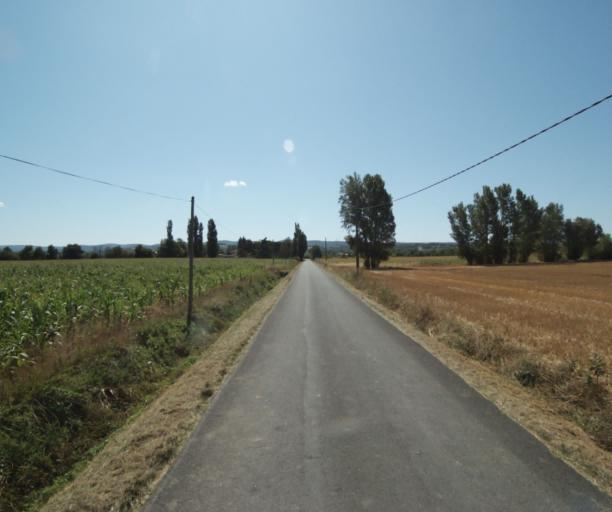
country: FR
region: Midi-Pyrenees
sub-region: Departement de la Haute-Garonne
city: Revel
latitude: 43.4614
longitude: 1.9702
